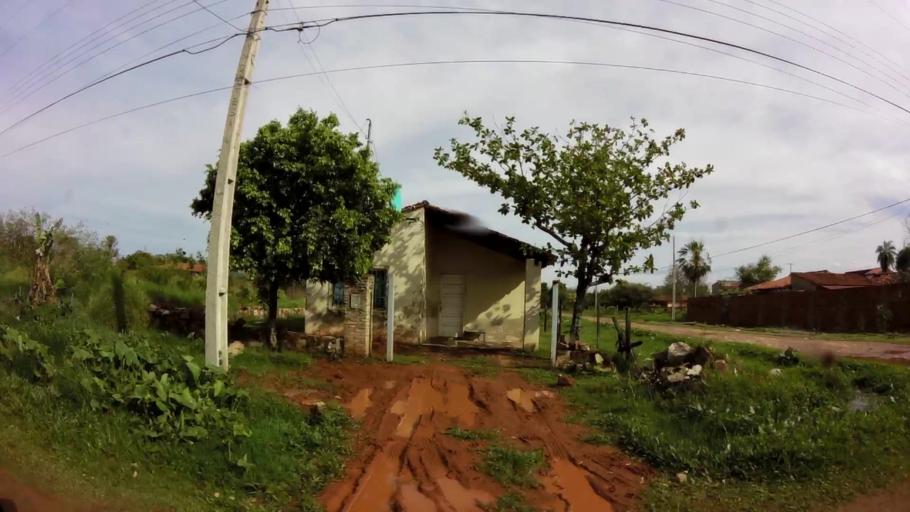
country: PY
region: Central
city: Limpio
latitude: -25.1774
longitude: -57.4951
